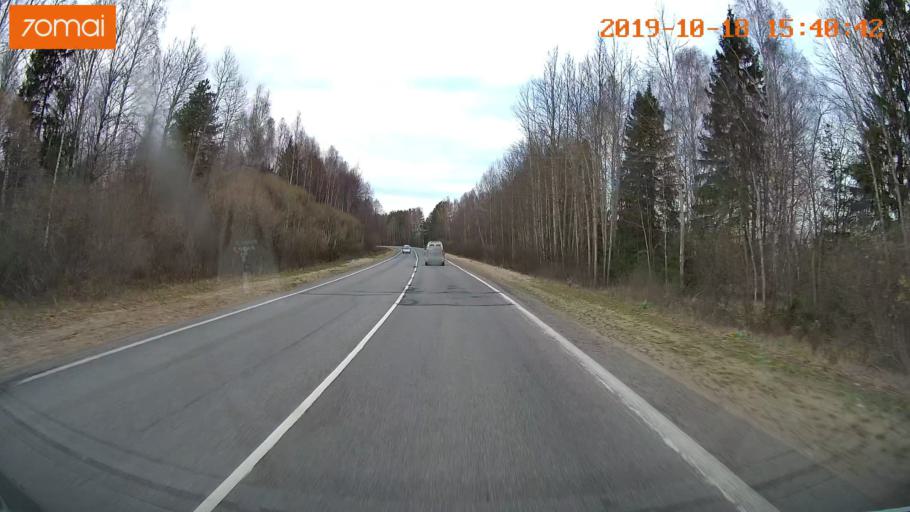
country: RU
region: Vladimir
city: Golovino
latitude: 55.9376
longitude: 40.5922
